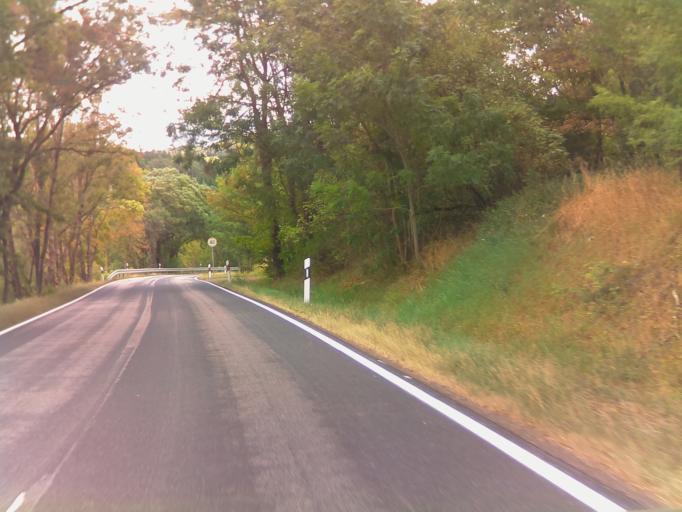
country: DE
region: Thuringia
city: Vachdorf
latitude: 50.5331
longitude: 10.5437
